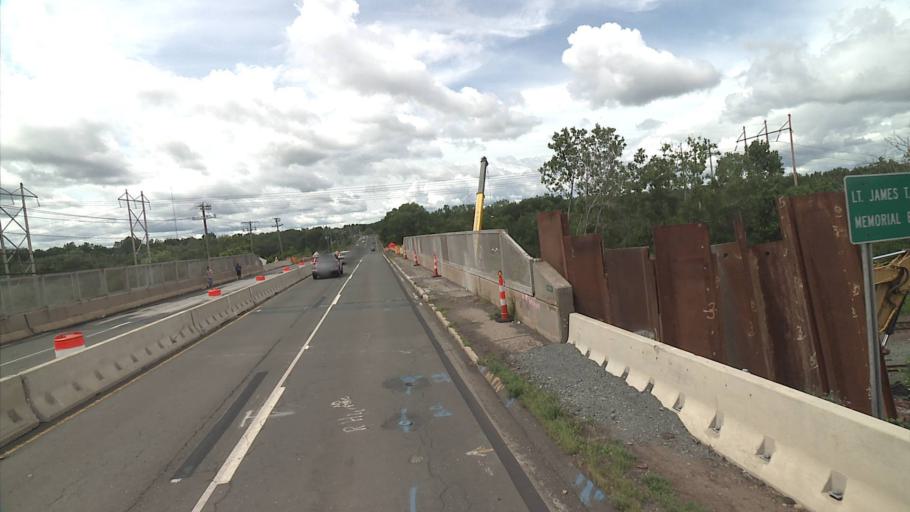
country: US
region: Connecticut
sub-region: Hartford County
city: Newington
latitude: 41.6948
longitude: -72.7487
